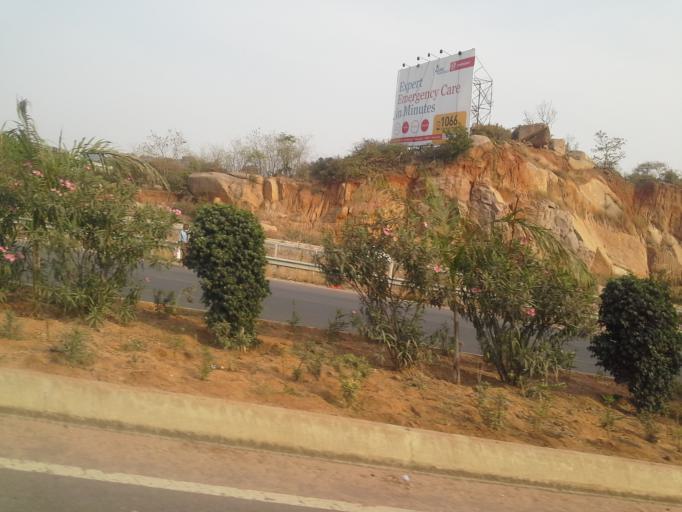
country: IN
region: Telangana
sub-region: Rangareddi
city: Kukatpalli
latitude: 17.4106
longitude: 78.3545
